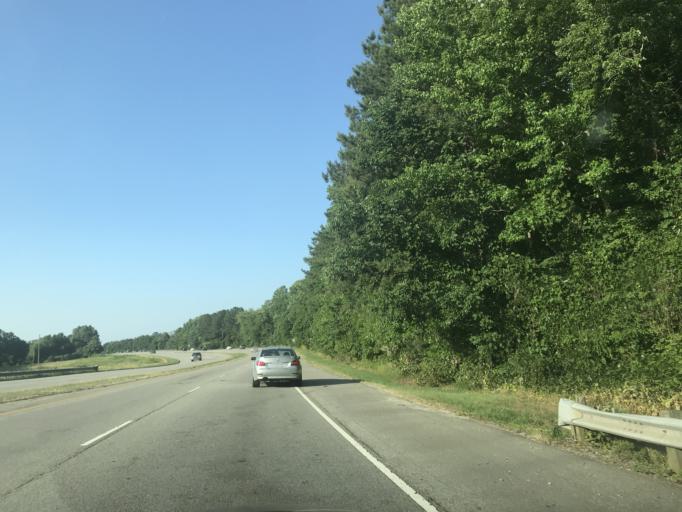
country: US
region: North Carolina
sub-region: Wake County
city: Raleigh
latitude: 35.7444
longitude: -78.6396
